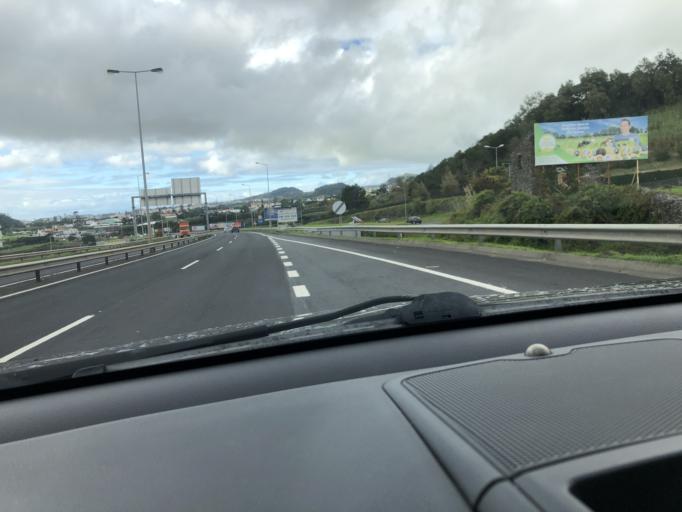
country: PT
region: Azores
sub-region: Ponta Delgada
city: Rosto de Cao
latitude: 37.7589
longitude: -25.6233
